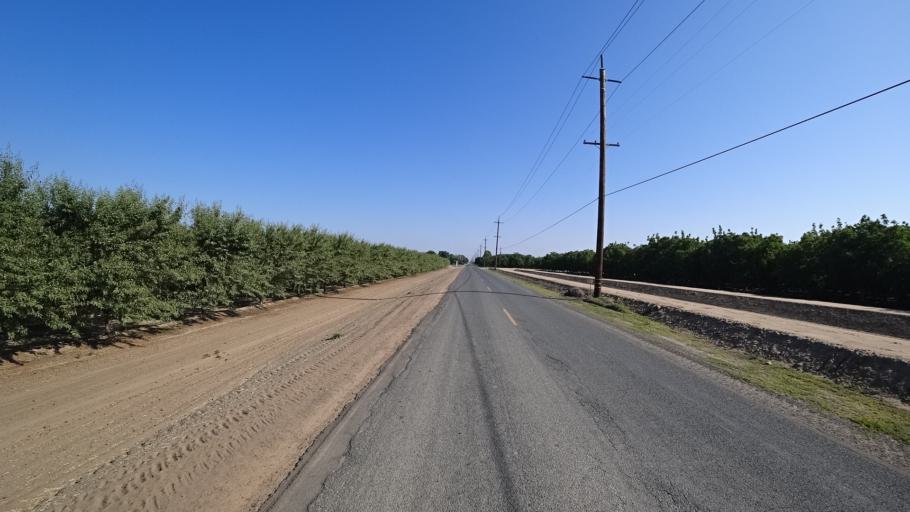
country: US
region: California
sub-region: Kings County
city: Home Garden
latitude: 36.2749
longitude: -119.5831
